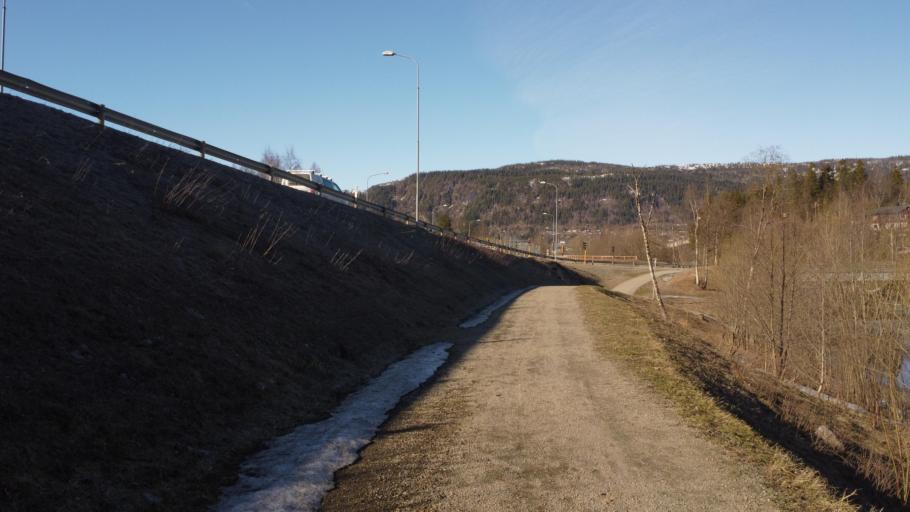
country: NO
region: Nordland
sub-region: Rana
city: Mo i Rana
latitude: 66.3154
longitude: 14.1676
